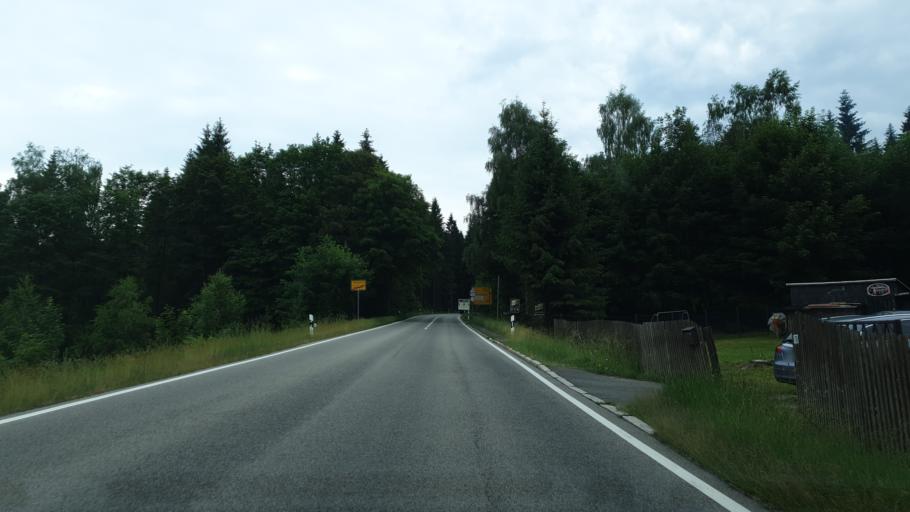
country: DE
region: Saxony
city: Auerbach
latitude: 50.4843
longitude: 12.4338
